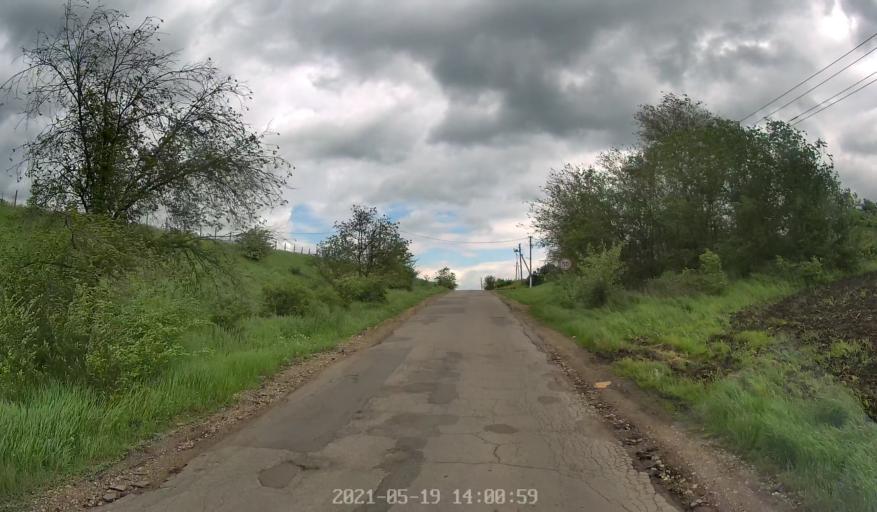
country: MD
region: Chisinau
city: Chisinau
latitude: 47.0332
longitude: 28.9345
